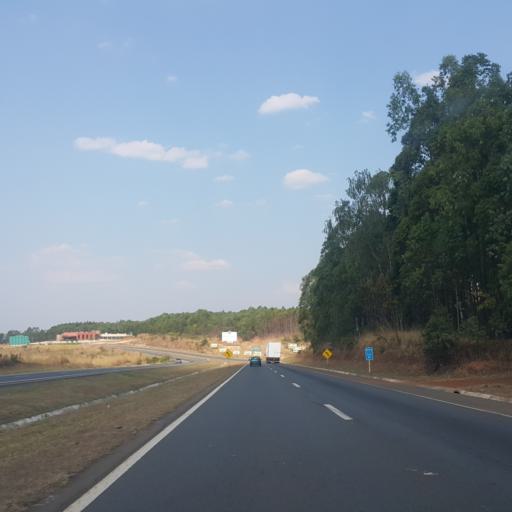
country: BR
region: Goias
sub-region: Abadiania
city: Abadiania
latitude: -16.1901
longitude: -48.6792
